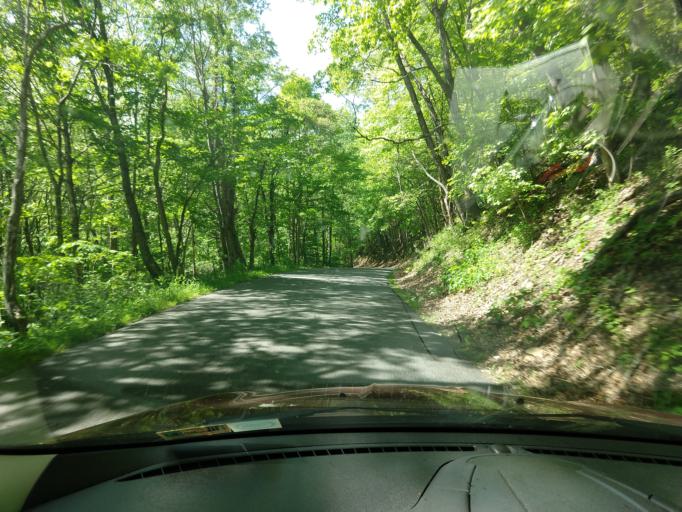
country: US
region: Virginia
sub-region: City of Covington
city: Fairlawn
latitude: 37.7136
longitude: -79.9116
